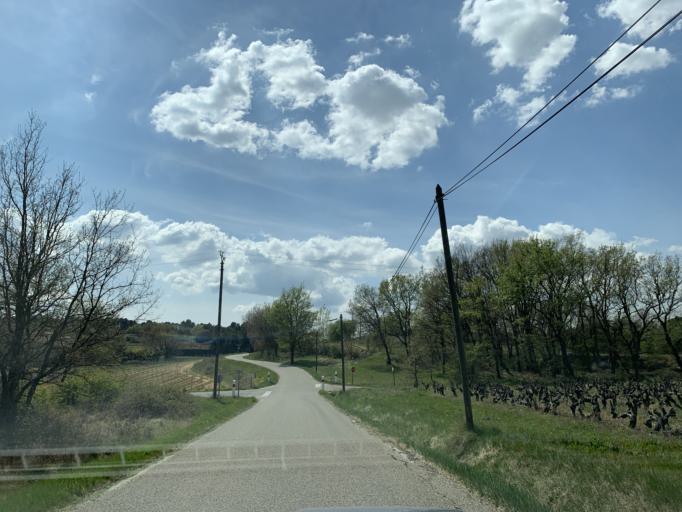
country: FR
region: Provence-Alpes-Cote d'Azur
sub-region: Departement du Vaucluse
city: Roussillon
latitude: 43.8840
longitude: 5.2706
